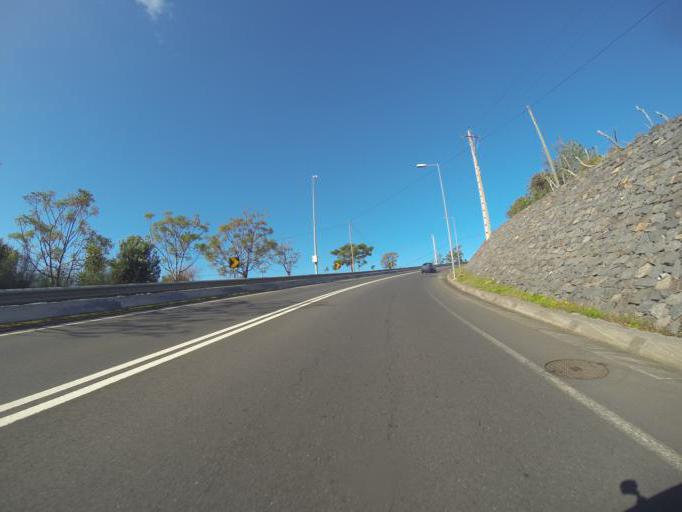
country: PT
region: Madeira
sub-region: Calheta
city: Estreito da Calheta
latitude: 32.7322
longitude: -17.1907
